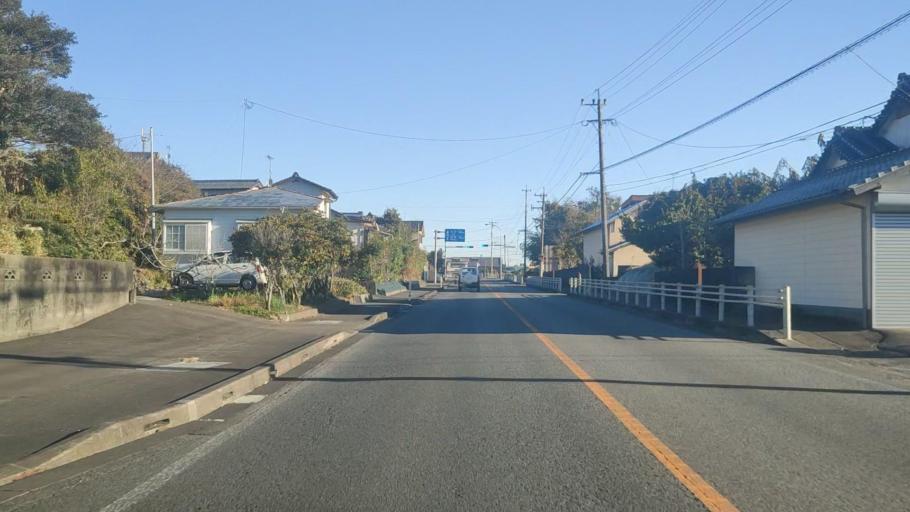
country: JP
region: Miyazaki
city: Nobeoka
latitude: 32.3706
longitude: 131.6296
